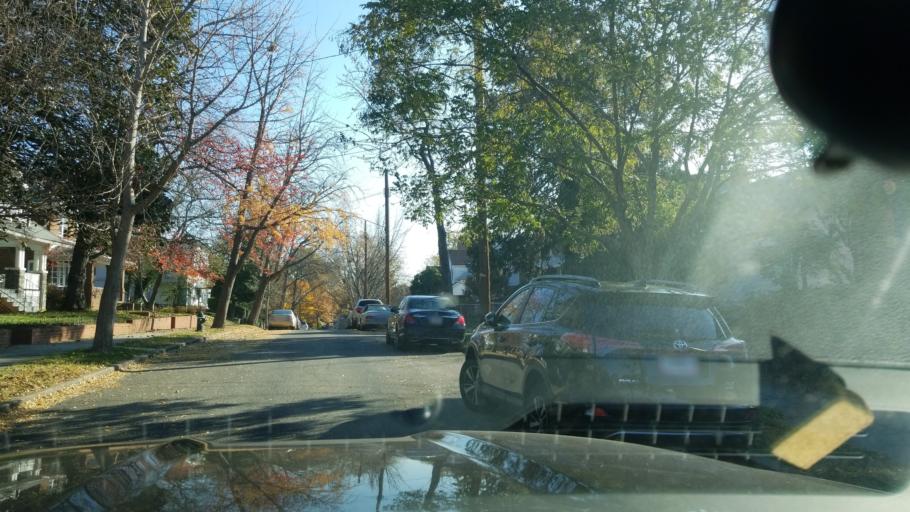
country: US
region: Maryland
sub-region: Montgomery County
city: Takoma Park
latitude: 38.9595
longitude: -77.0108
